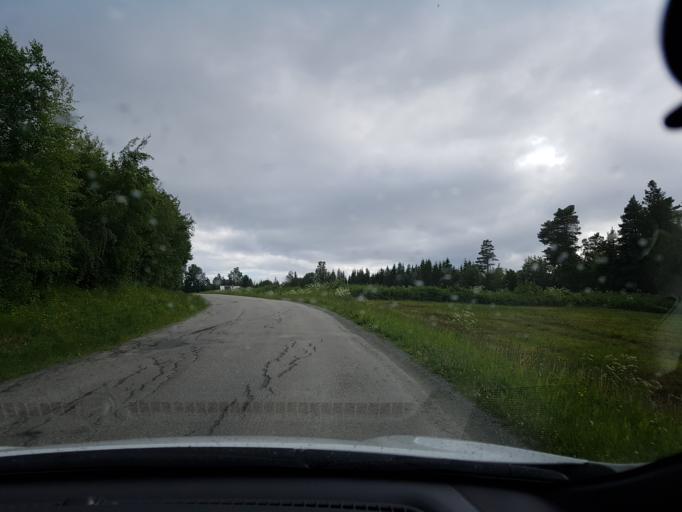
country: NO
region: Nord-Trondelag
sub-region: Frosta
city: Frosta
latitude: 63.6102
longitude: 10.7398
